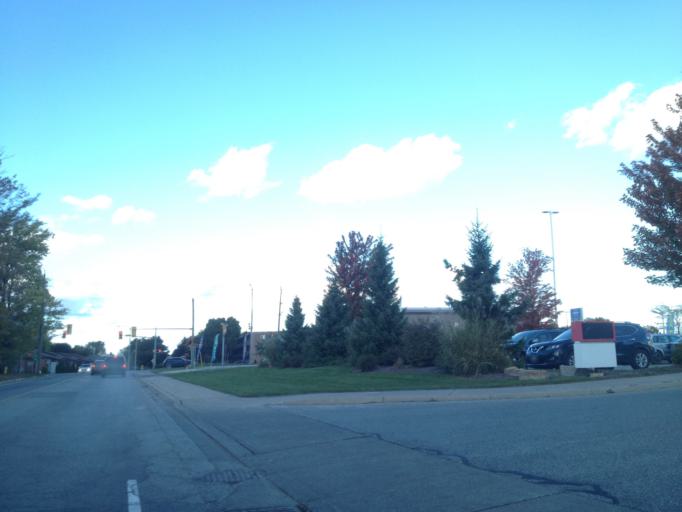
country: CA
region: Ontario
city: Amherstburg
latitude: 42.0376
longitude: -82.7276
